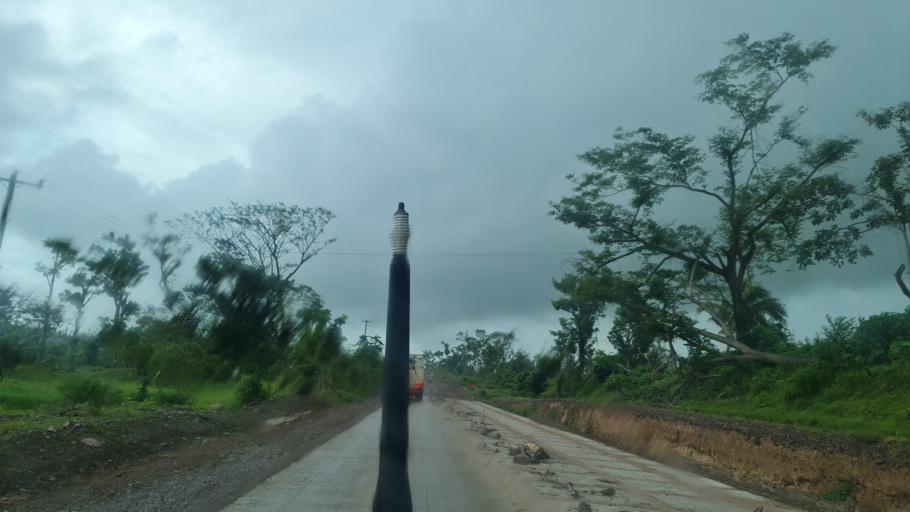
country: NI
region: Atlantico Norte (RAAN)
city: Siuna
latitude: 13.7049
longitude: -84.4459
